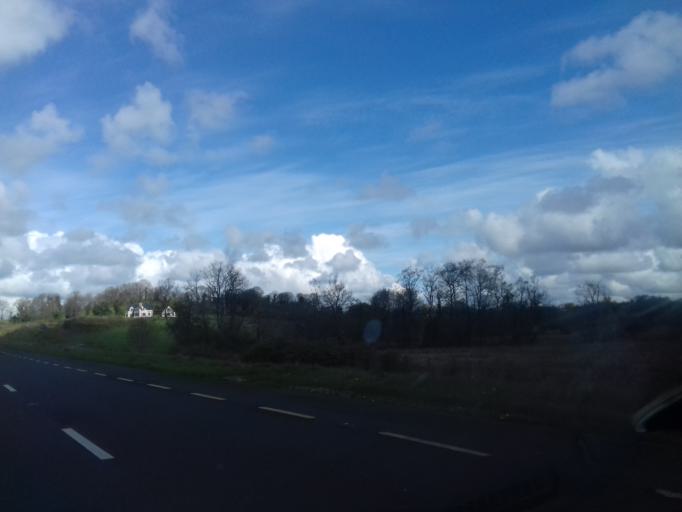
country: IE
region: Ulster
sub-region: An Cabhan
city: Belturbet
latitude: 54.0751
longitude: -7.4179
